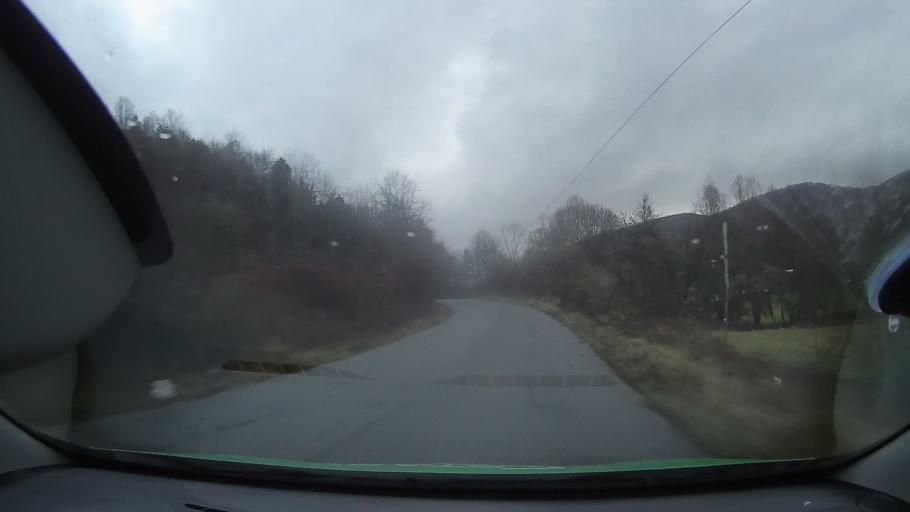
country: RO
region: Hunedoara
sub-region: Comuna Baia de Cris
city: Baia de Cris
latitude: 46.2069
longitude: 22.7160
